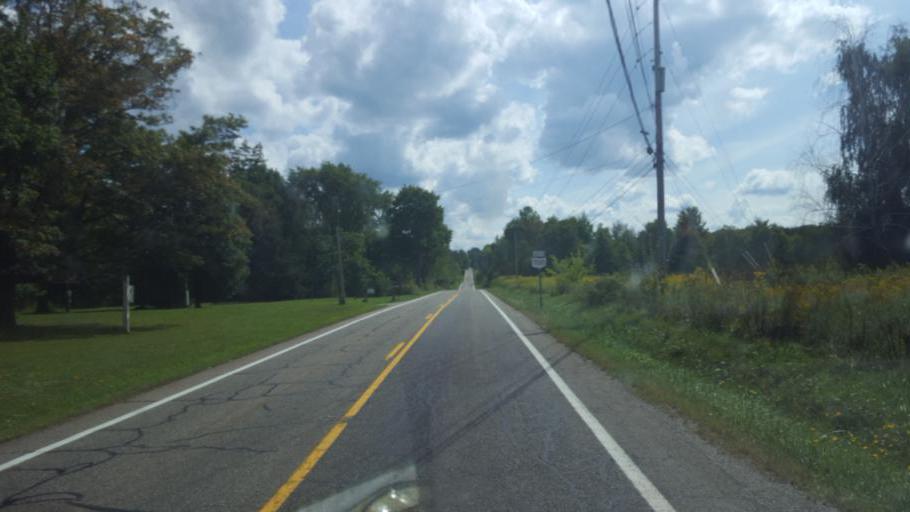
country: US
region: Ohio
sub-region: Portage County
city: Hiram
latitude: 41.3453
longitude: -81.1431
